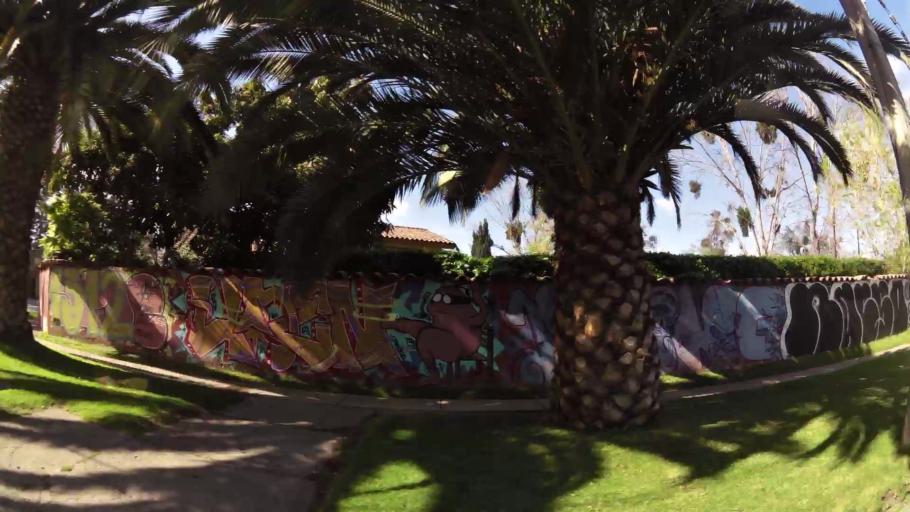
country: CL
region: Santiago Metropolitan
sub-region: Provincia de Santiago
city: Villa Presidente Frei, Nunoa, Santiago, Chile
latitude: -33.4469
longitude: -70.5635
